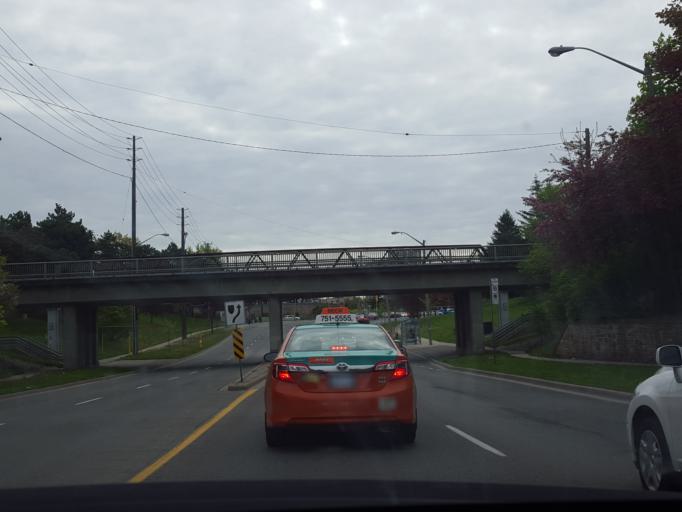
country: CA
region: Ontario
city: Willowdale
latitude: 43.7896
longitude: -79.3713
